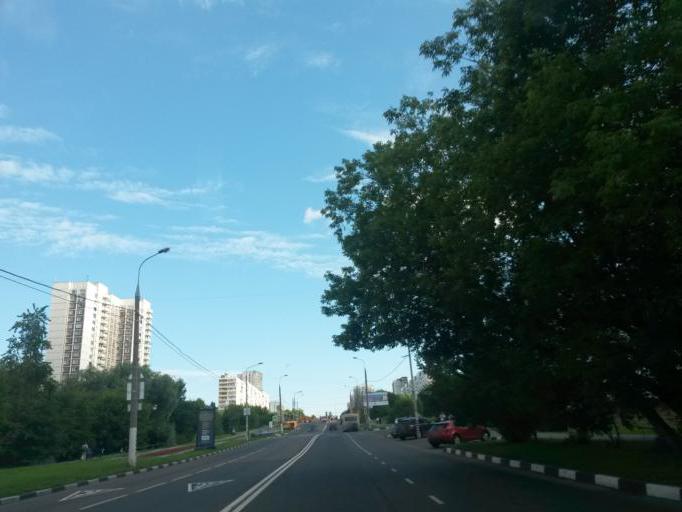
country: RU
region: Moscow
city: Orekhovo-Borisovo
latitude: 55.6295
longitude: 37.7418
